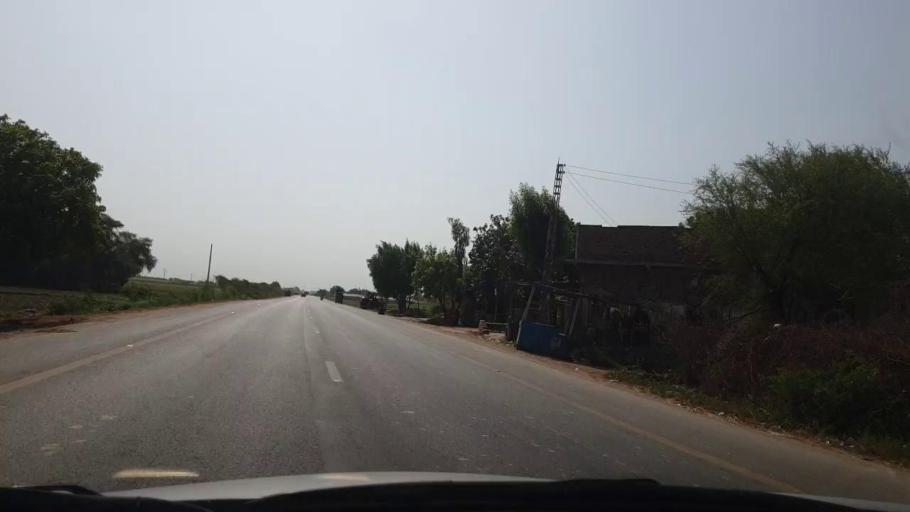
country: PK
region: Sindh
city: Tando Muhammad Khan
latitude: 25.1190
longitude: 68.5722
